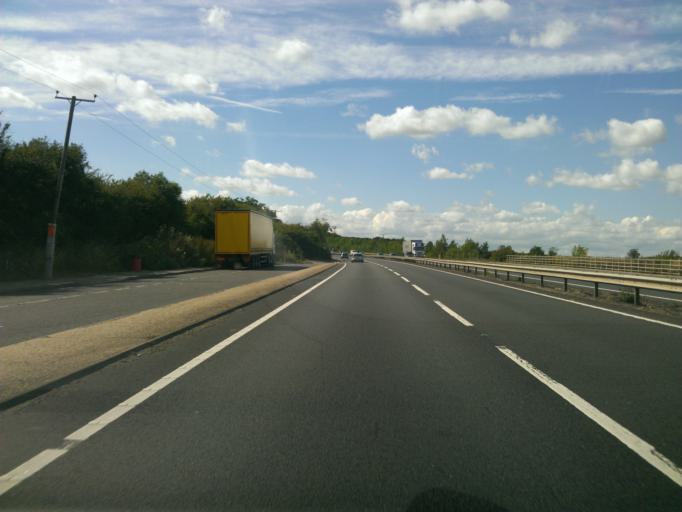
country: GB
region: England
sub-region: Northamptonshire
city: Thrapston
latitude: 52.3790
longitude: -0.4757
